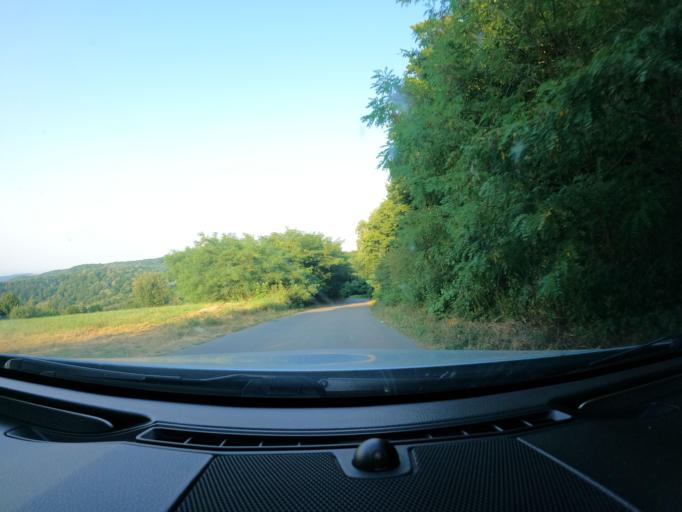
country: RS
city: Vrdnik
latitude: 45.1566
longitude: 19.7499
